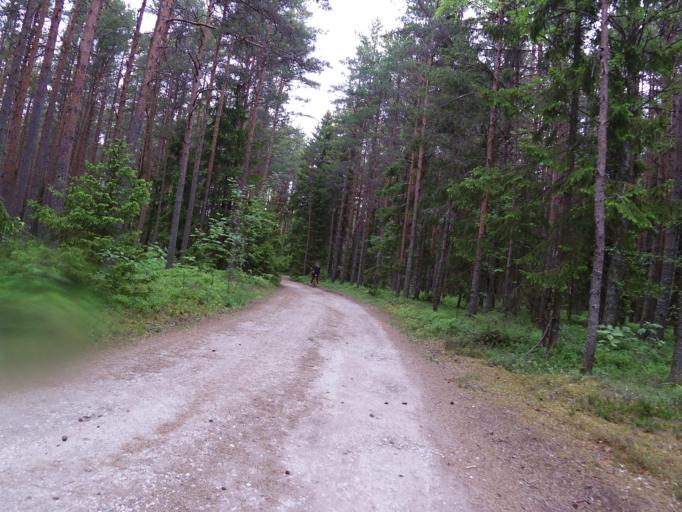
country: EE
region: Harju
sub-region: Paldiski linn
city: Paldiski
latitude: 59.2503
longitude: 23.7495
